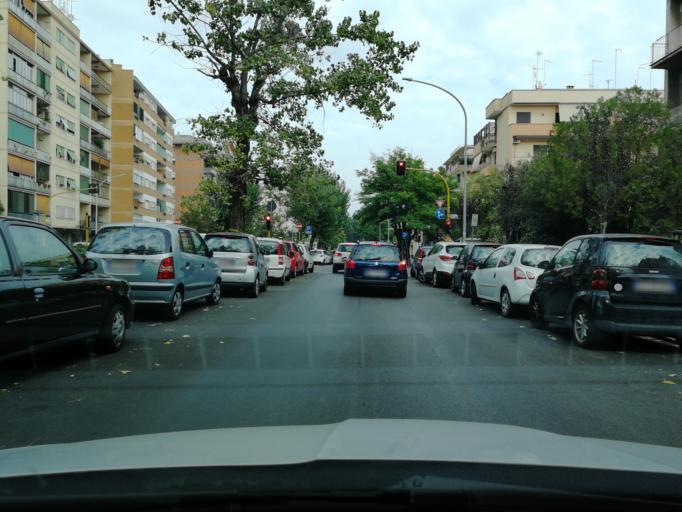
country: IT
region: Latium
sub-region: Citta metropolitana di Roma Capitale
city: Ciampino
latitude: 41.8524
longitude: 12.5663
